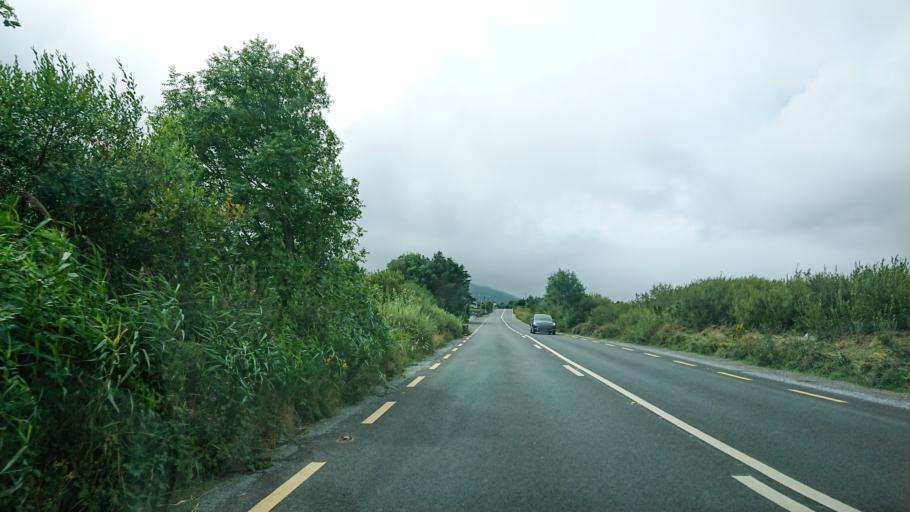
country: IE
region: Munster
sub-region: Ciarrai
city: Cahersiveen
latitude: 51.9632
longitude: -10.1785
